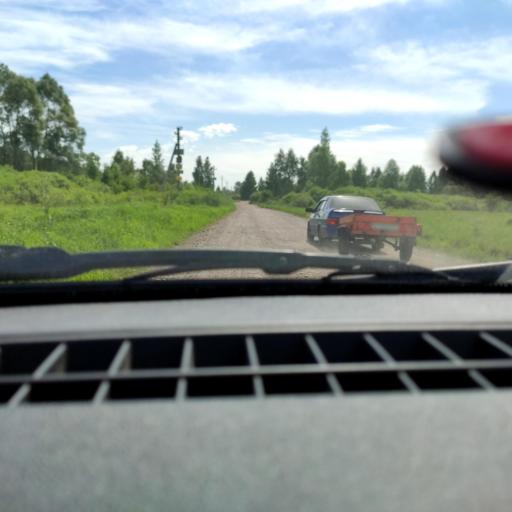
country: RU
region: Bashkortostan
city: Kabakovo
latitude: 54.7328
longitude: 56.2003
